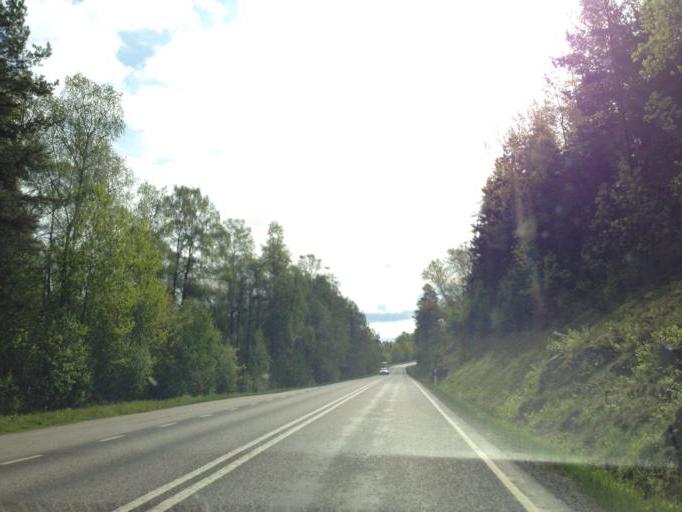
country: SE
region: Soedermanland
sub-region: Nykopings Kommun
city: Stigtomta
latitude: 58.9723
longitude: 16.8435
